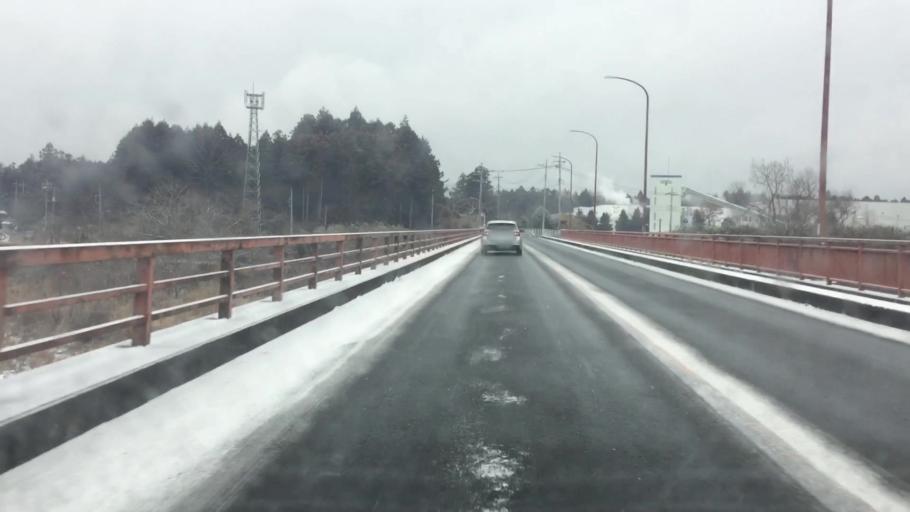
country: JP
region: Tochigi
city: Imaichi
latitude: 36.7434
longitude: 139.7480
